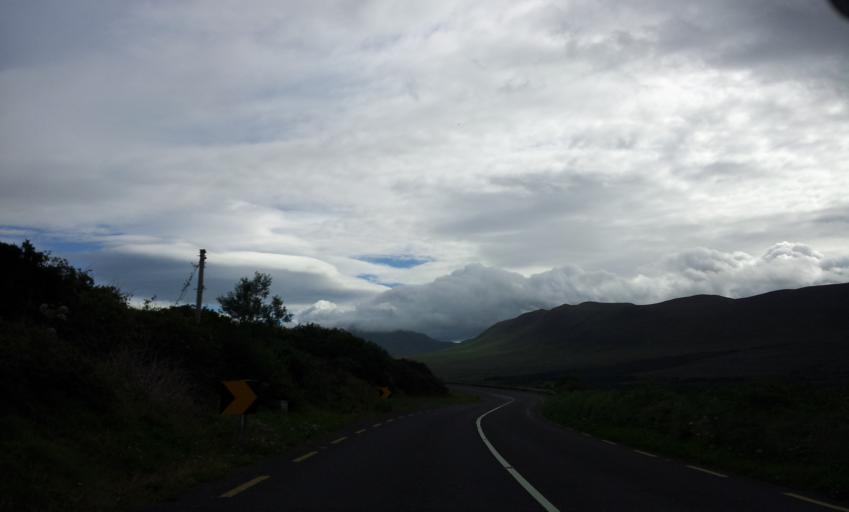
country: IE
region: Munster
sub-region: Ciarrai
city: Killorglin
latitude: 52.1729
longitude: -9.9968
